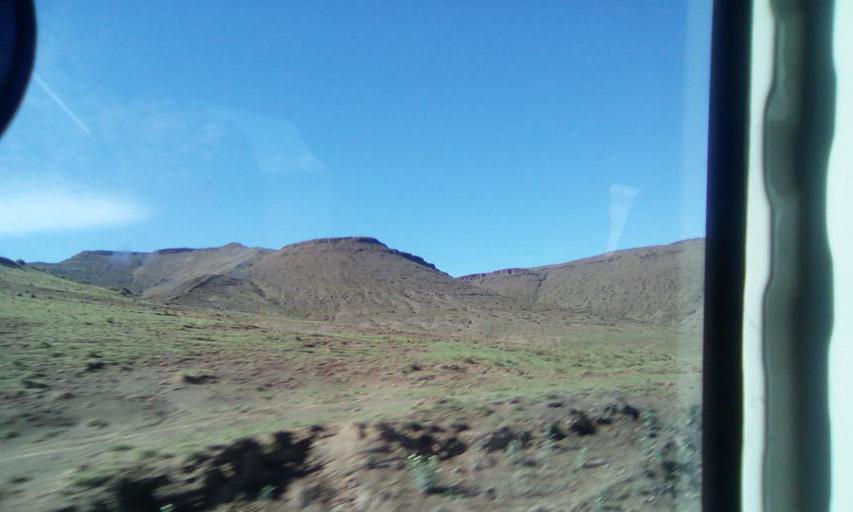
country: LS
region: Qacha's Nek
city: Qacha's Nek
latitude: -30.0423
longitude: 28.2738
